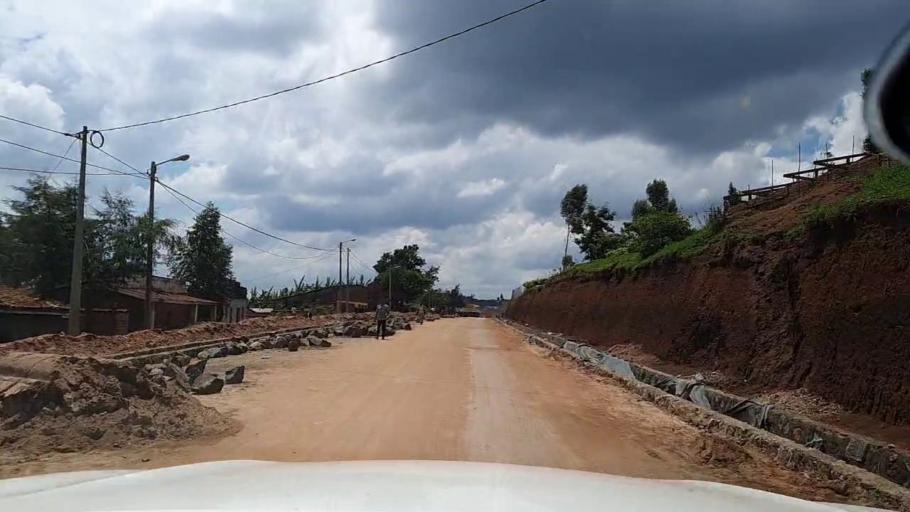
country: RW
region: Southern Province
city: Butare
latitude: -2.6935
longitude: 29.5689
